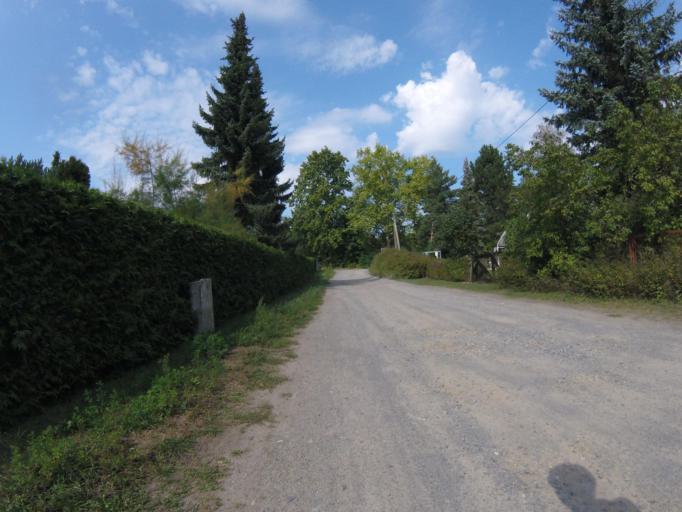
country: DE
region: Brandenburg
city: Bestensee
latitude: 52.2592
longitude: 13.6569
